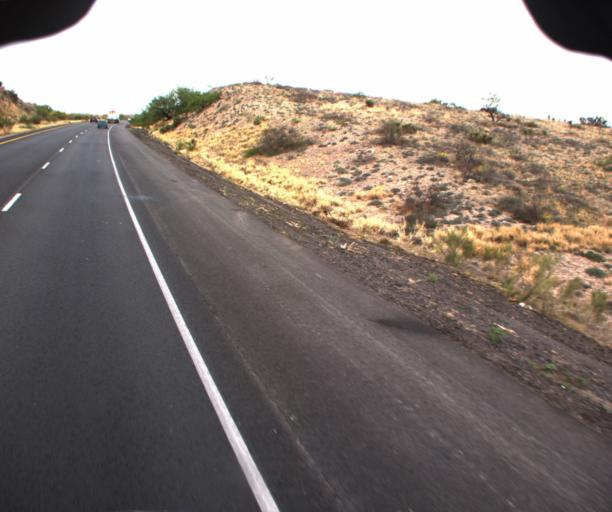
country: US
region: Arizona
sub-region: Pima County
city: Vail
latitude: 31.9970
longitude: -110.6549
